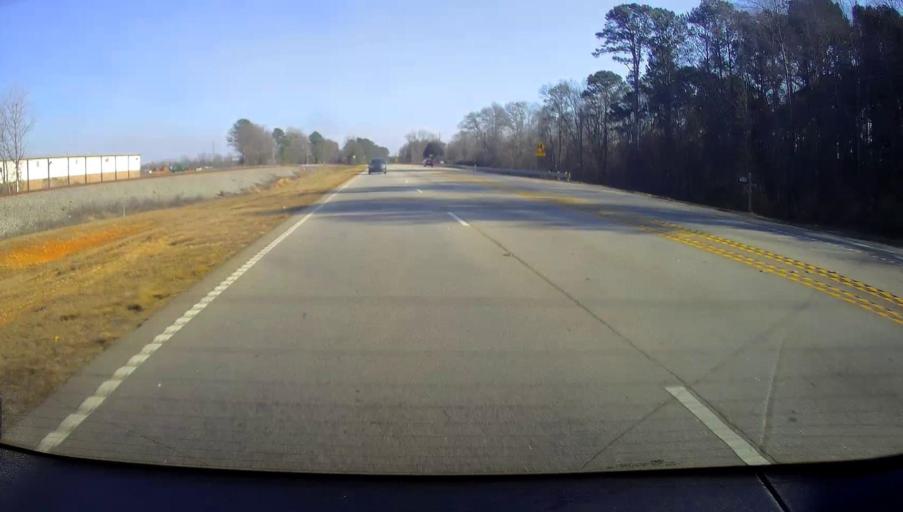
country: US
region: Georgia
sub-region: Butts County
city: Jackson
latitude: 33.3203
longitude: -83.9919
